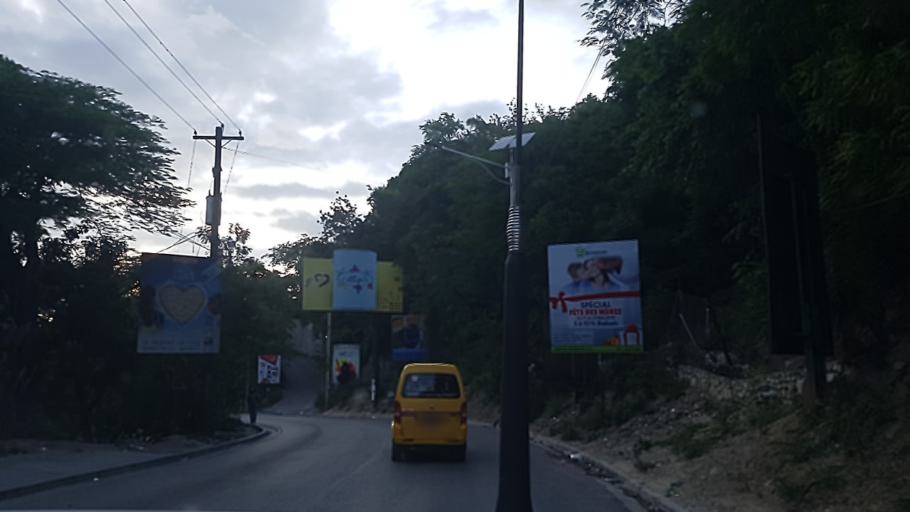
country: HT
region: Ouest
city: Petionville
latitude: 18.5255
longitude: -72.2974
